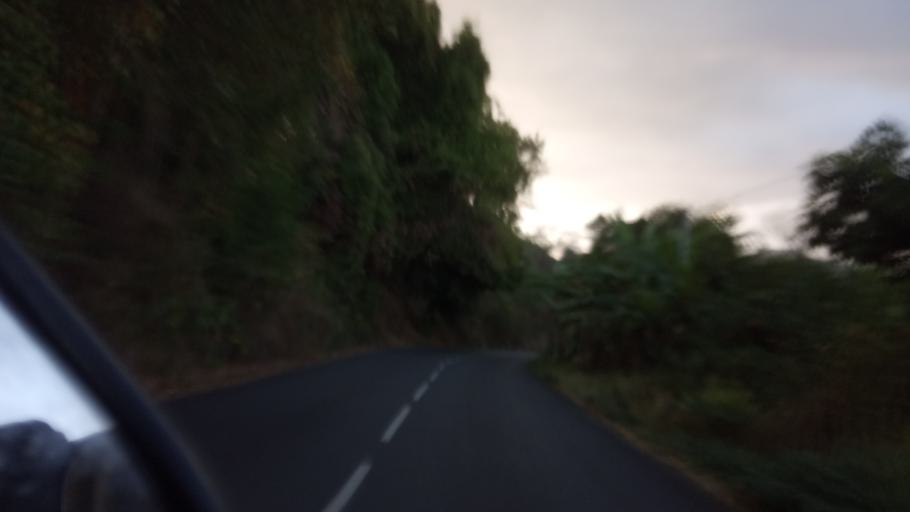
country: YT
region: Kani-Keli
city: Kani Keli
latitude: -12.9280
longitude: 45.1158
